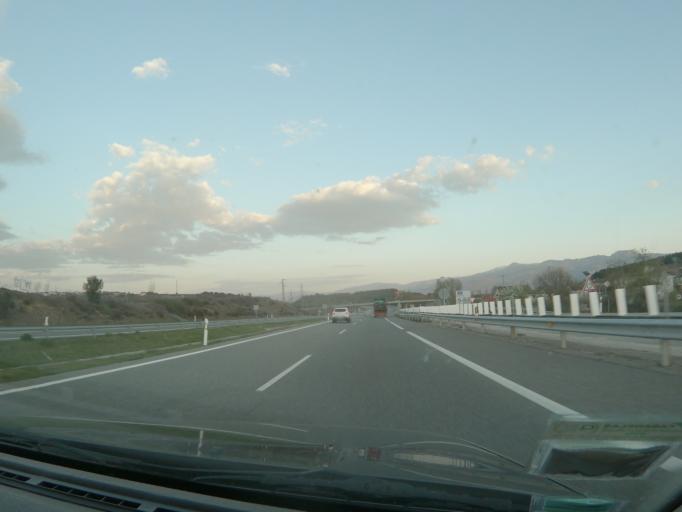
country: ES
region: Castille and Leon
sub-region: Provincia de Leon
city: Villadecanes
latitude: 42.5763
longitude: -6.7762
